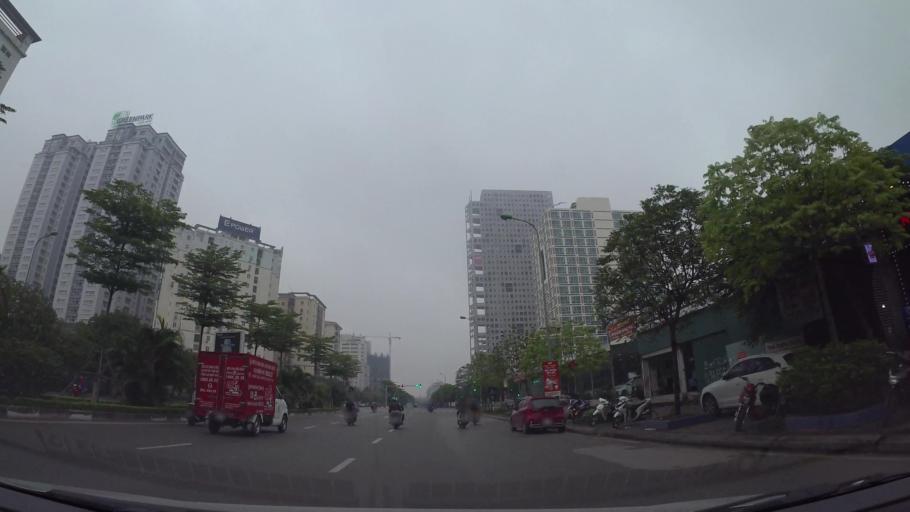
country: VN
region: Ha Noi
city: Cau Giay
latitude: 21.0208
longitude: 105.7867
